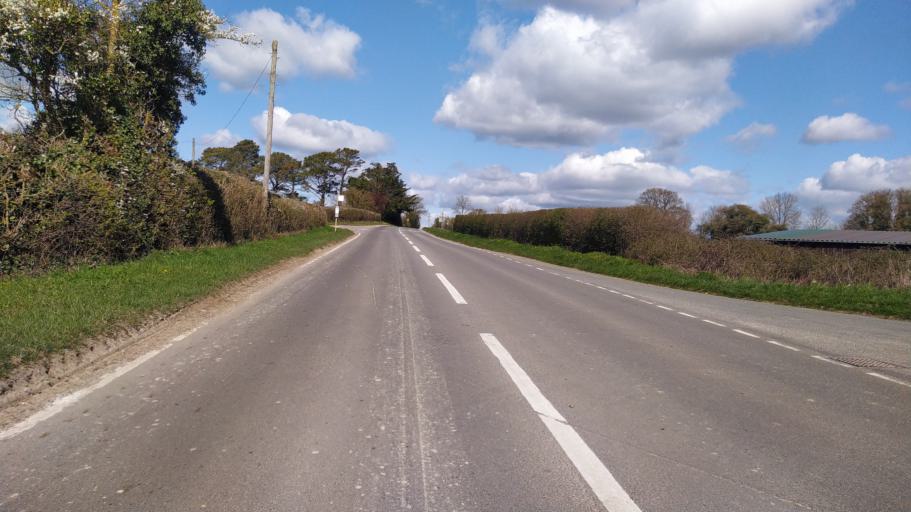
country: GB
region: England
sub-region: Dorset
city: Manston
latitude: 50.9777
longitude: -2.2901
